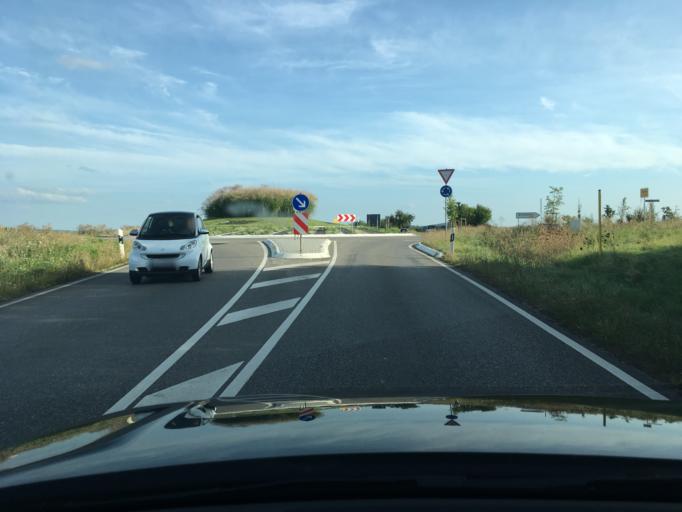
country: DE
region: Baden-Wuerttemberg
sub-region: Regierungsbezirk Stuttgart
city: Affalterbach
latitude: 48.9169
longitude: 9.3327
